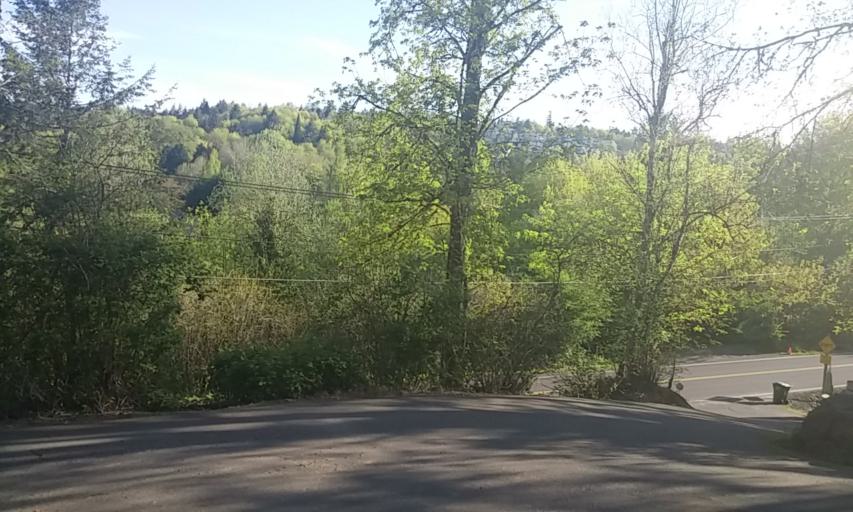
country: US
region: Oregon
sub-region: Washington County
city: Cedar Mill
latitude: 45.5453
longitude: -122.7869
